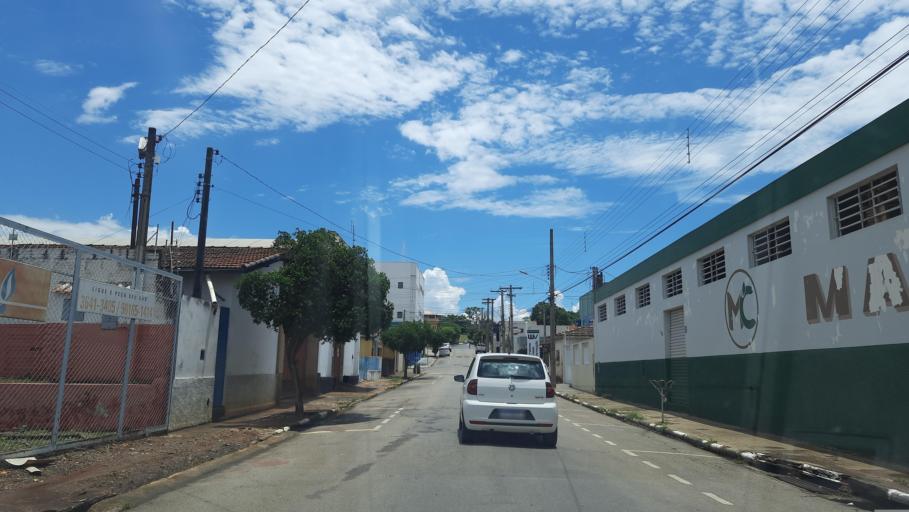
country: BR
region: Sao Paulo
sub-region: Vargem Grande Do Sul
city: Vargem Grande do Sul
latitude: -21.8399
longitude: -46.9009
